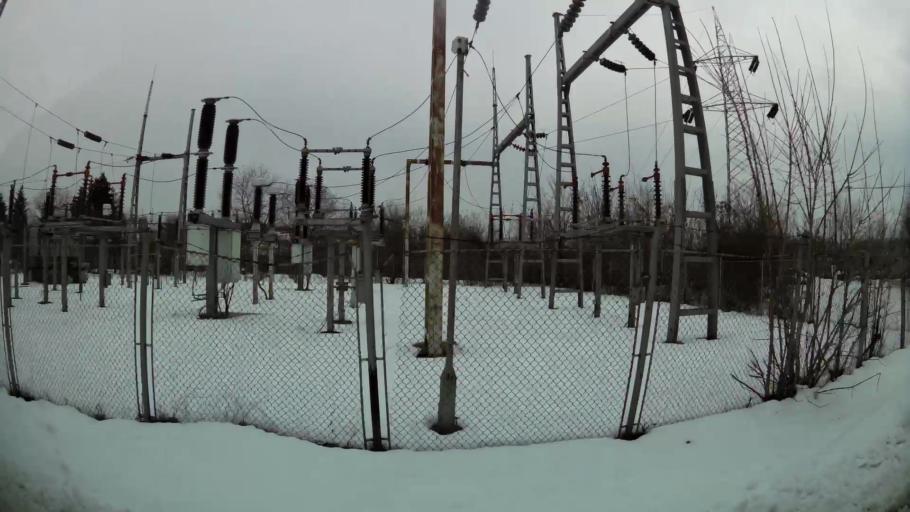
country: RS
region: Central Serbia
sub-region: Belgrade
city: Zemun
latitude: 44.8348
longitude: 20.3765
